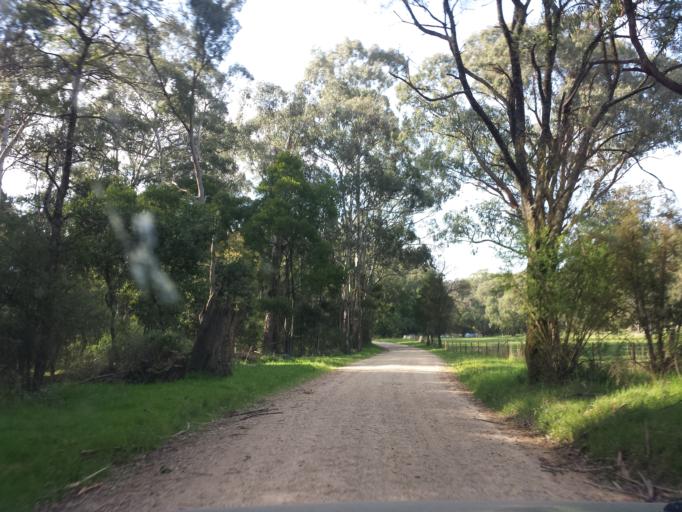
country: AU
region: Victoria
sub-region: Murrindindi
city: Alexandra
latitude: -37.3414
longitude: 145.7473
